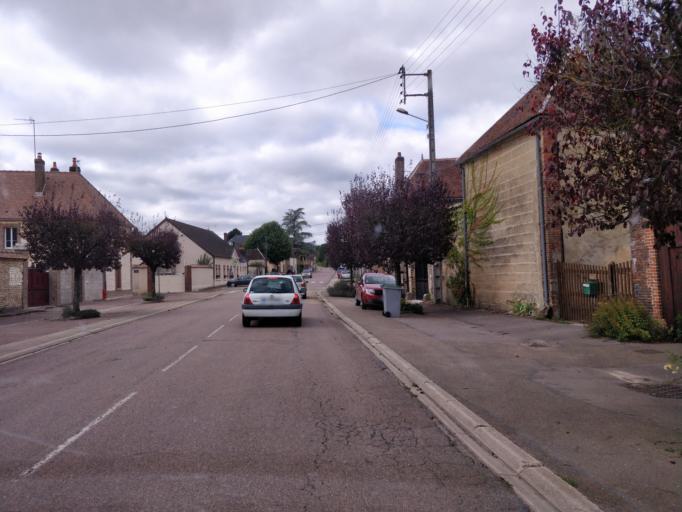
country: FR
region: Bourgogne
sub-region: Departement de l'Yonne
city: Saint-Florentin
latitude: 48.0840
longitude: 3.7009
